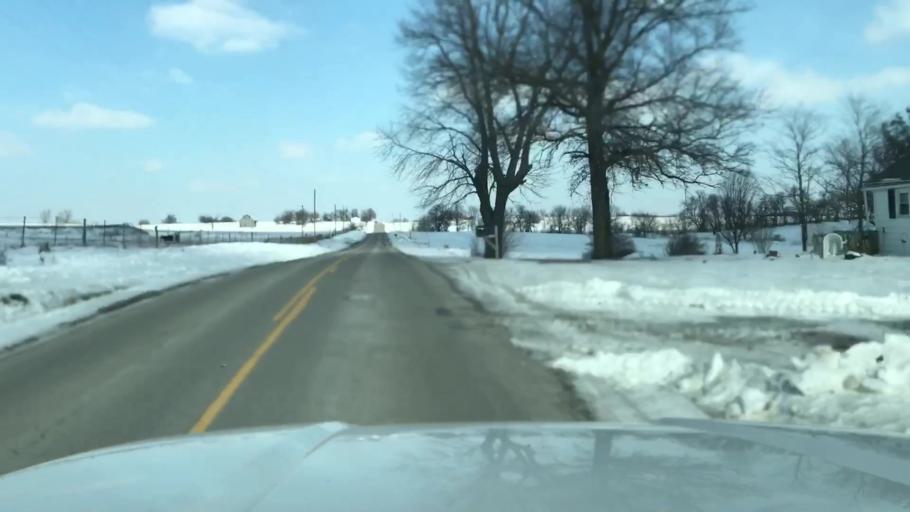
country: US
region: Missouri
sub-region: Nodaway County
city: Maryville
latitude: 40.3479
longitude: -94.7224
